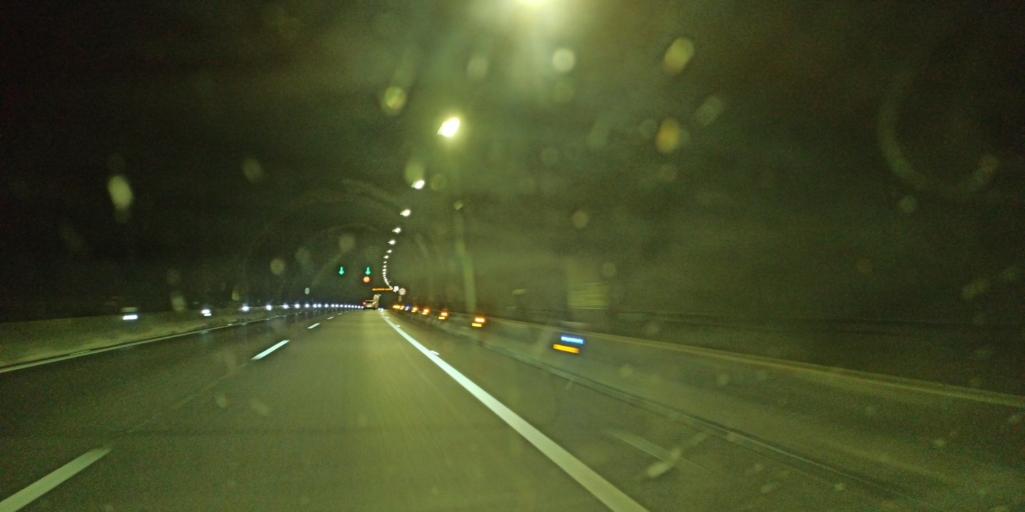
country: ES
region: Catalonia
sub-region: Provincia de Barcelona
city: Sitges
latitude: 41.2456
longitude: 1.8364
